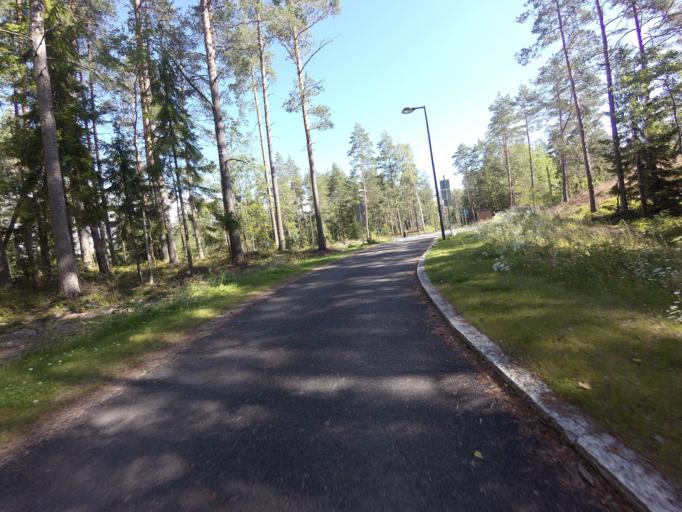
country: FI
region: Uusimaa
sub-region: Helsinki
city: Espoo
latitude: 60.1490
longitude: 24.5929
